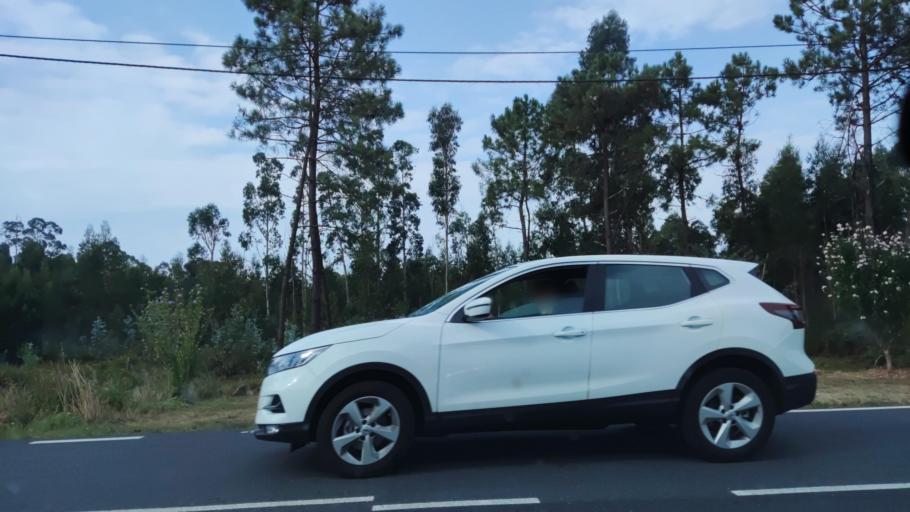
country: ES
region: Galicia
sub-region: Provincia de Pontevedra
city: Catoira
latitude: 42.6533
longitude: -8.7600
